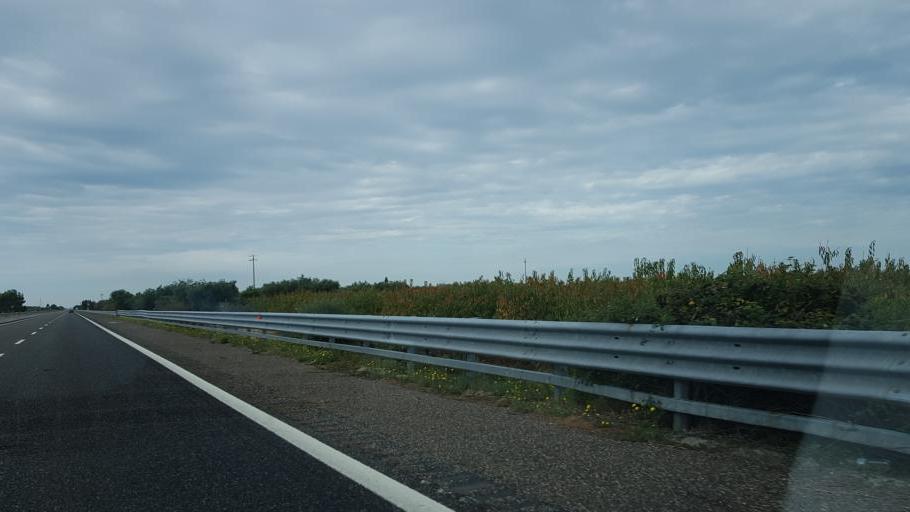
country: IT
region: Apulia
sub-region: Provincia di Barletta - Andria - Trani
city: Bisceglie
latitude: 41.1874
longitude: 16.5144
